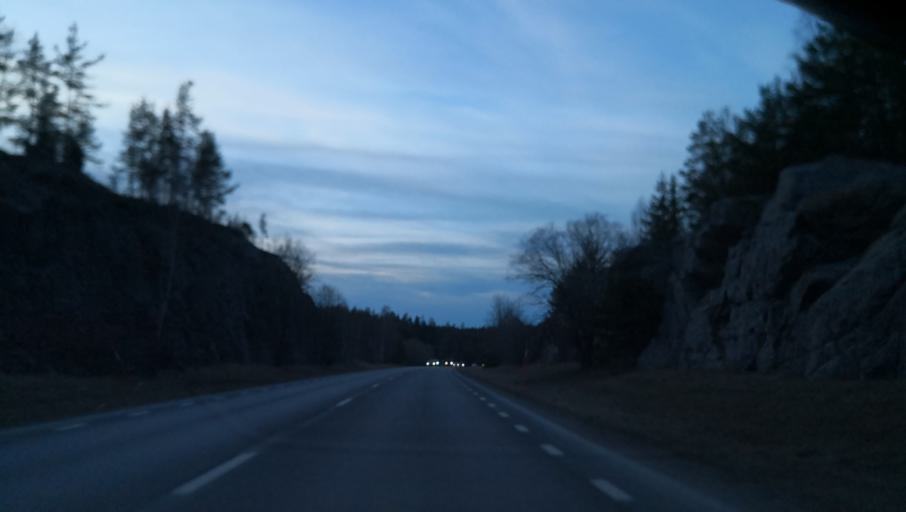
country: SE
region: Stockholm
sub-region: Varmdo Kommun
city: Gustavsberg
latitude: 59.2920
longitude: 18.3944
